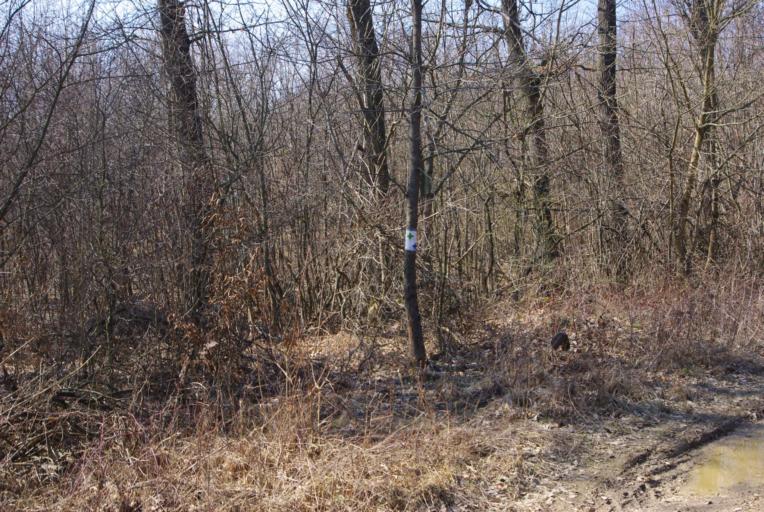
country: HU
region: Pest
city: Budakeszi
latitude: 47.5479
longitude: 18.8879
